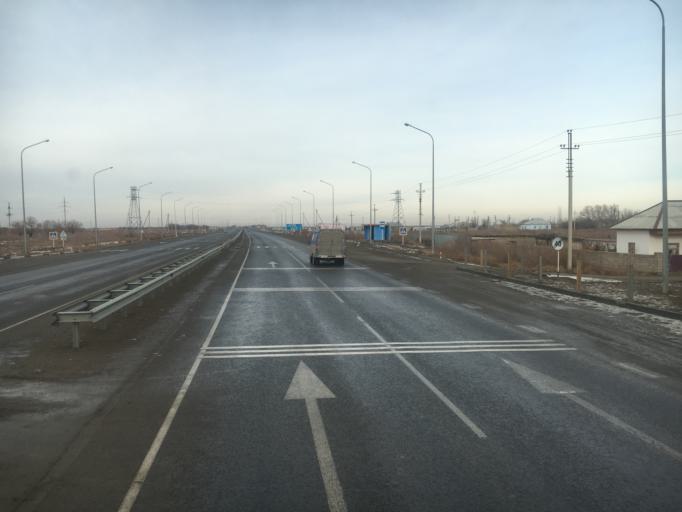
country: KZ
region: Qyzylorda
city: Shieli
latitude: 44.1381
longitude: 66.9679
